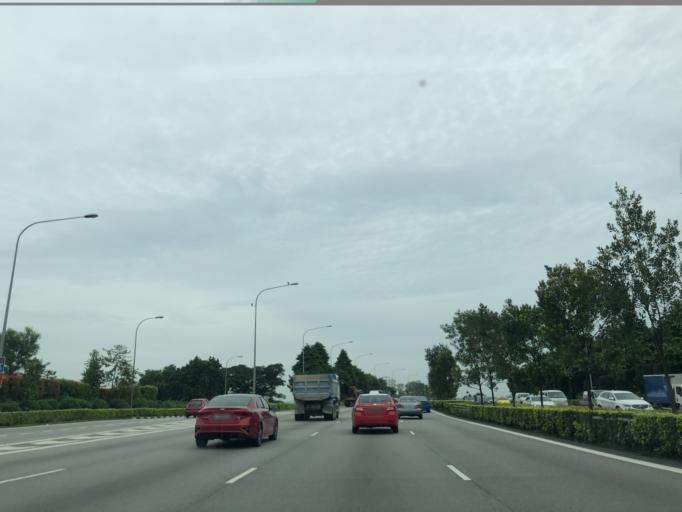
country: SG
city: Singapore
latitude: 1.3526
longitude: 103.8572
